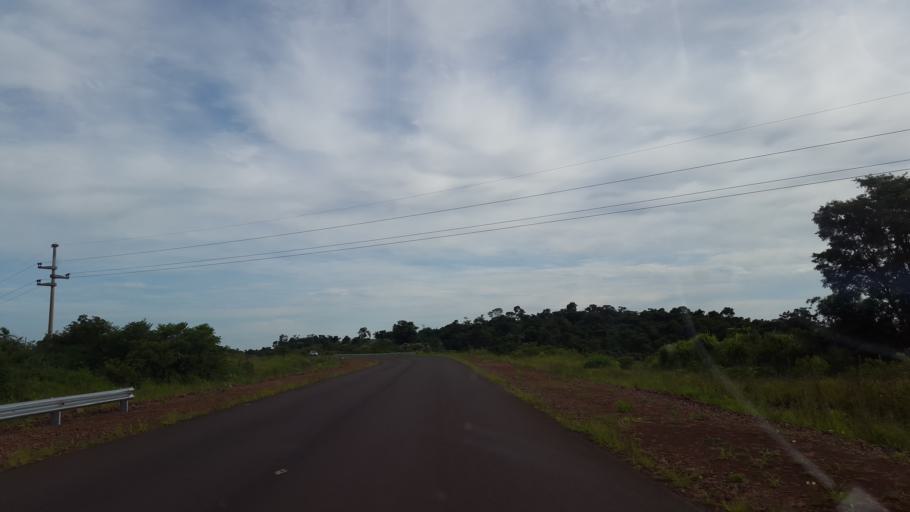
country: AR
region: Misiones
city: Bernardo de Irigoyen
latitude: -26.4162
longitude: -53.8239
